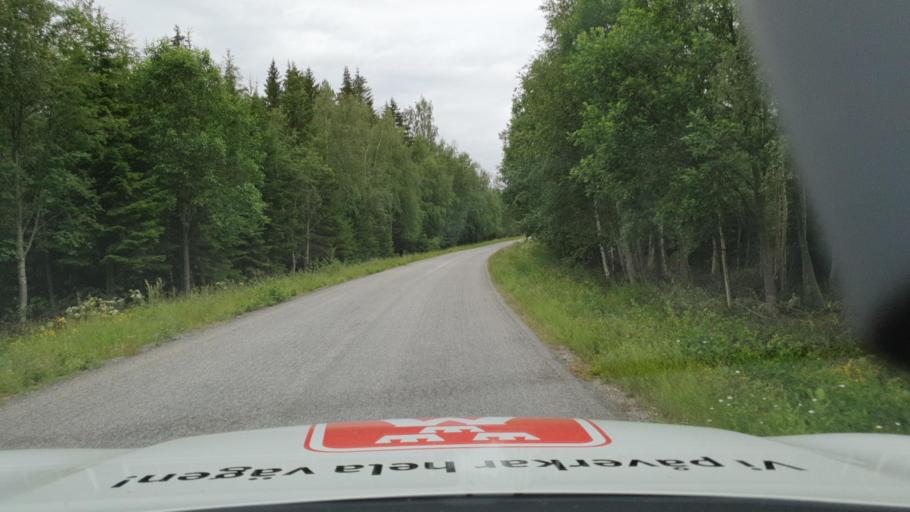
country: SE
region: Vaesterbotten
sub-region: Nordmalings Kommun
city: Nordmaling
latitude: 63.5290
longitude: 19.4231
